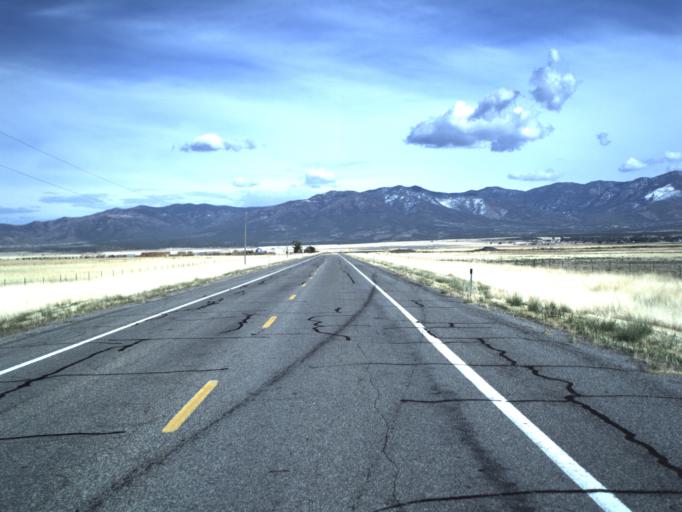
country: US
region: Utah
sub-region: Millard County
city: Fillmore
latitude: 39.1181
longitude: -112.3226
